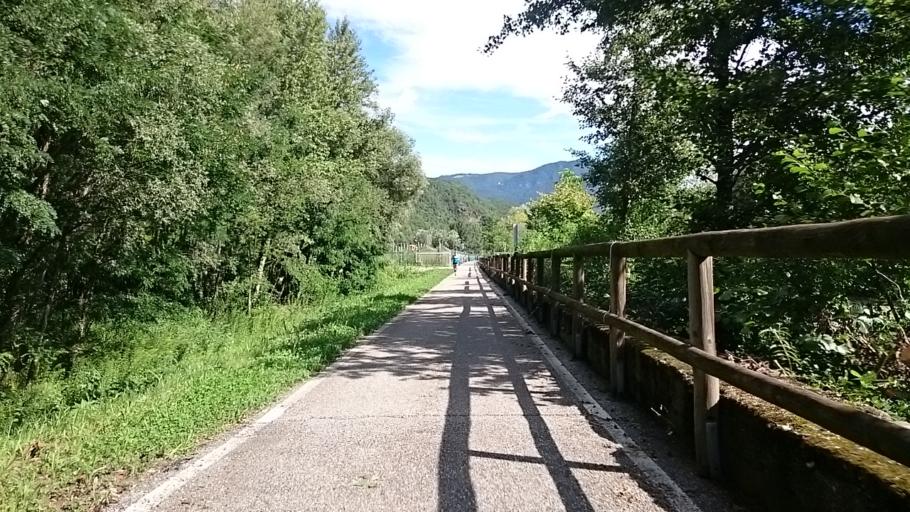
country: IT
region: Trentino-Alto Adige
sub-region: Bolzano
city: Cornaiano
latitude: 46.4584
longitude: 11.3021
